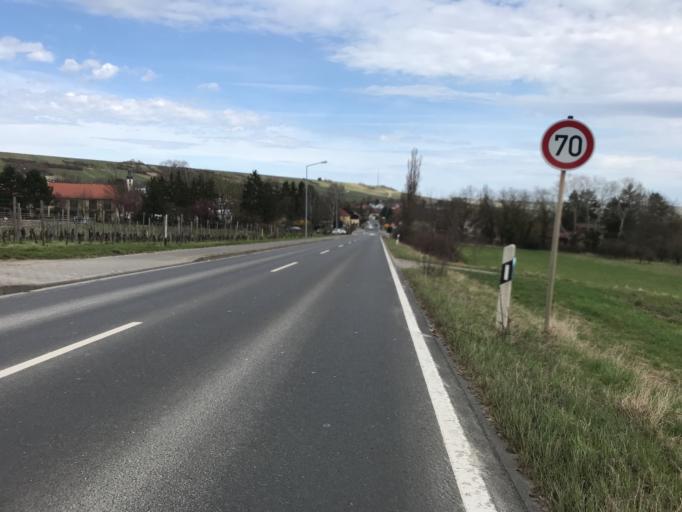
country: DE
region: Rheinland-Pfalz
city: Jugenheim
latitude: 49.8886
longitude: 8.0842
